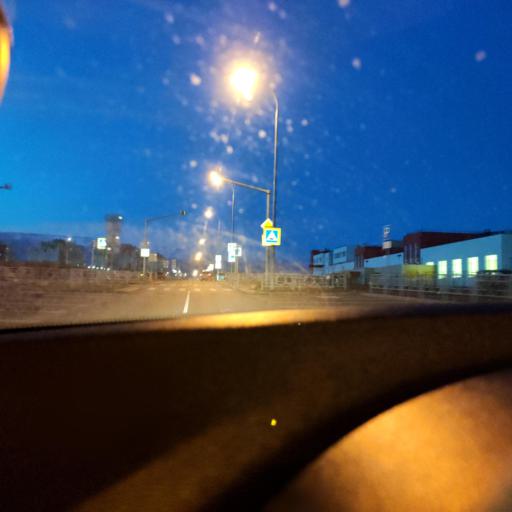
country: RU
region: Samara
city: Petra-Dubrava
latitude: 53.2969
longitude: 50.3289
